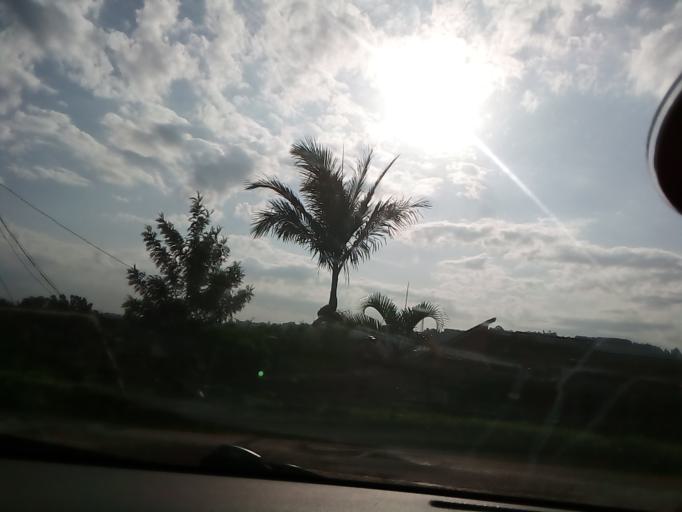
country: UG
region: Central Region
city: Masaka
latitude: -0.3501
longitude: 31.7424
